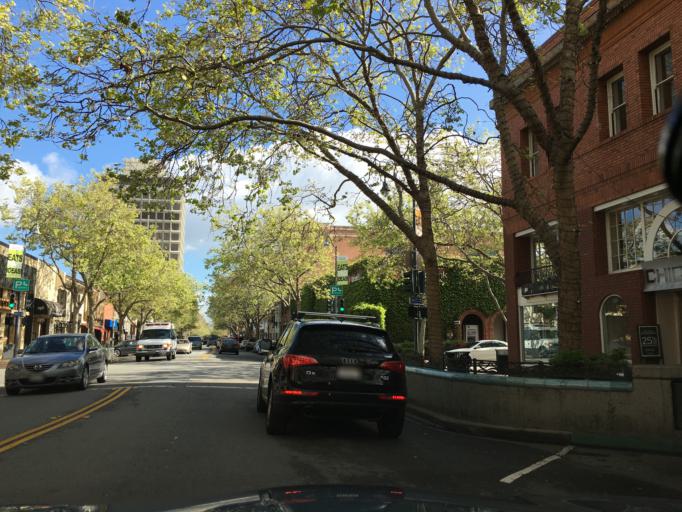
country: US
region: California
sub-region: Santa Clara County
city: Palo Alto
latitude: 37.4469
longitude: -122.1606
